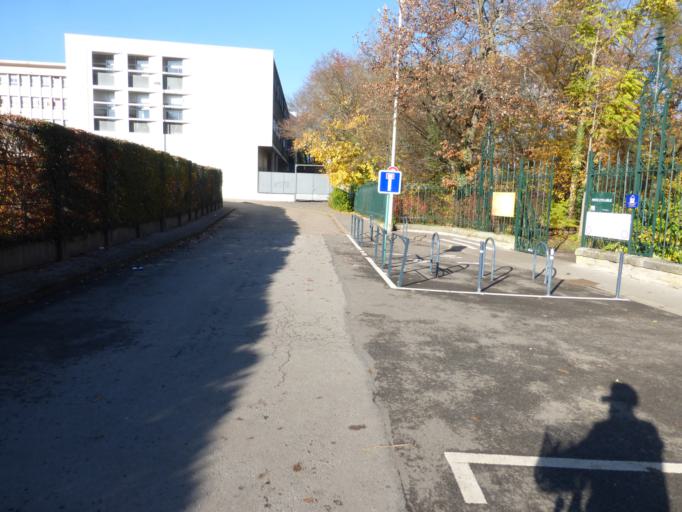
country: FR
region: Lorraine
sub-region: Departement de Meurthe-et-Moselle
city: Nancy
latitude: 48.6802
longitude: 6.1692
